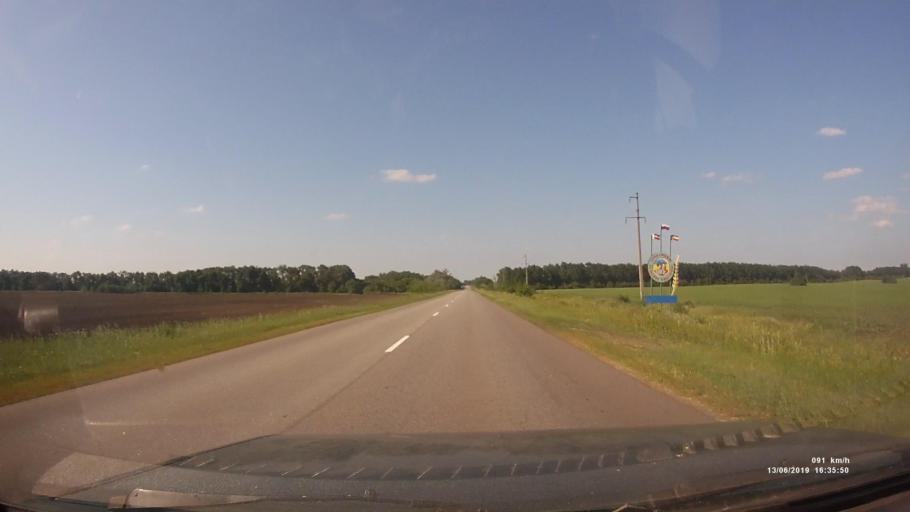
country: RU
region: Rostov
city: Kazanskaya
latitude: 49.8871
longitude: 41.3012
